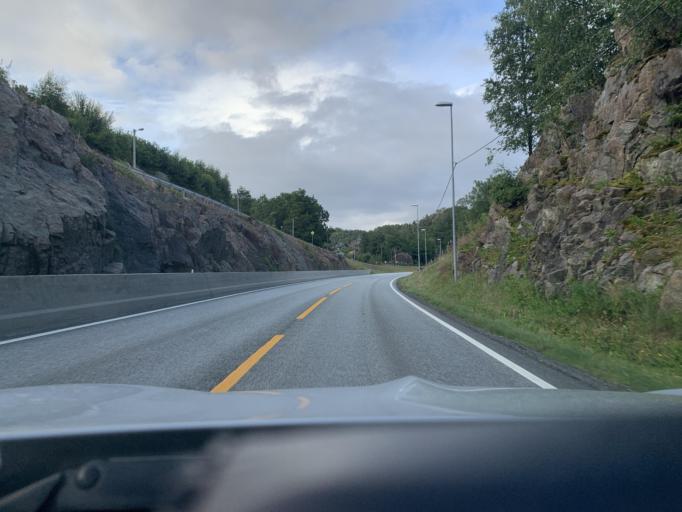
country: NO
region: Rogaland
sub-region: Bjerkreim
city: Vikesa
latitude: 58.5825
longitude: 6.0646
